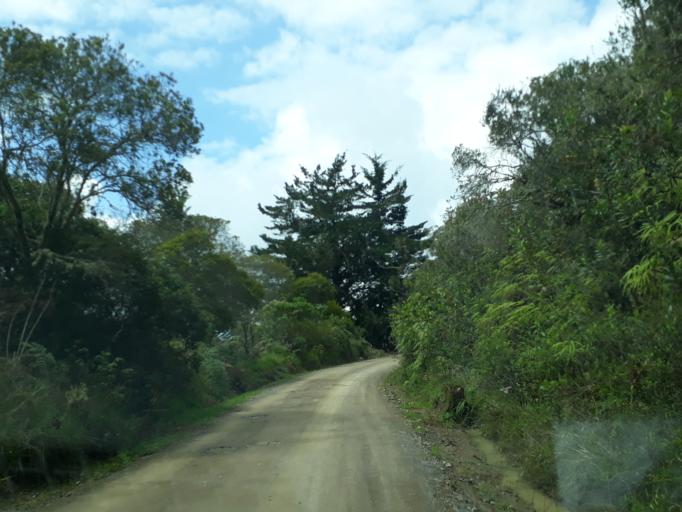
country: CO
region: Cundinamarca
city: Macheta
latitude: 5.1105
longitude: -73.5396
